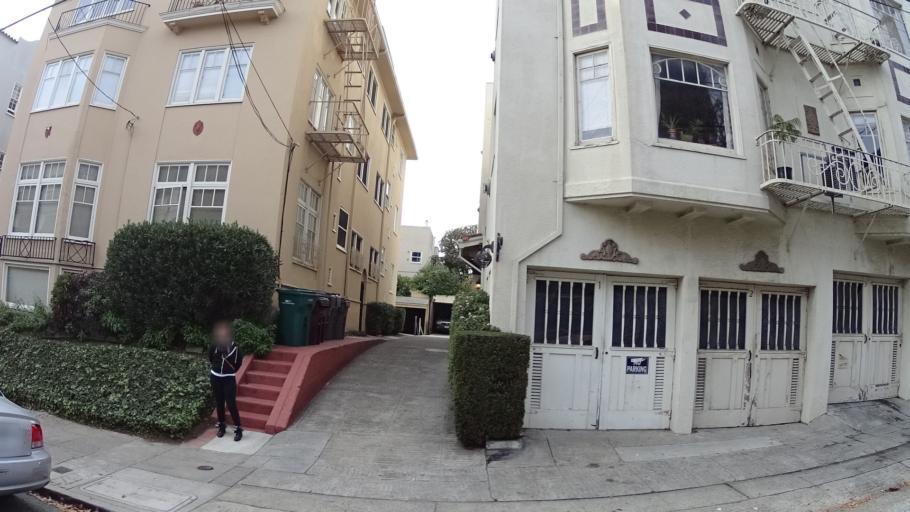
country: US
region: California
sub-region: Alameda County
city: Oakland
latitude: 37.8094
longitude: -122.2527
